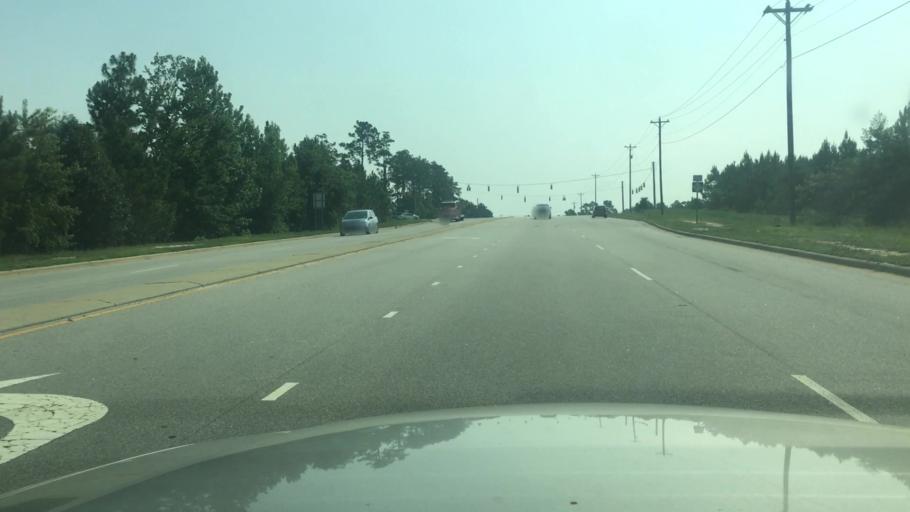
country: US
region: North Carolina
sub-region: Cumberland County
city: Hope Mills
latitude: 34.9901
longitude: -78.9508
